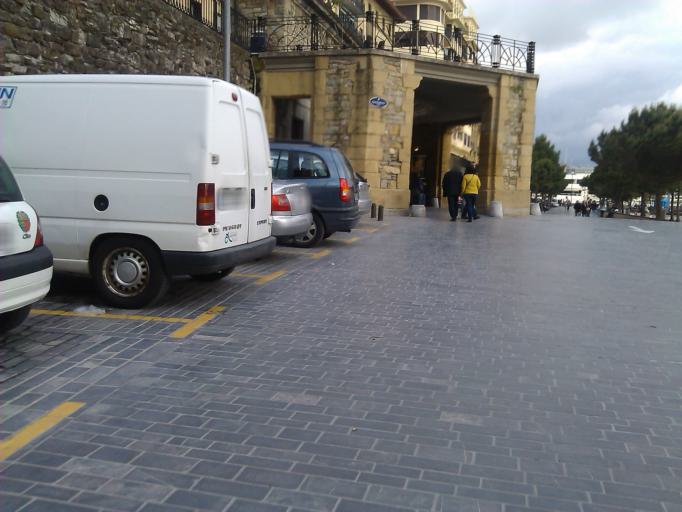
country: ES
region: Basque Country
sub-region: Provincia de Guipuzcoa
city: San Sebastian
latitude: 43.3233
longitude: -1.9875
